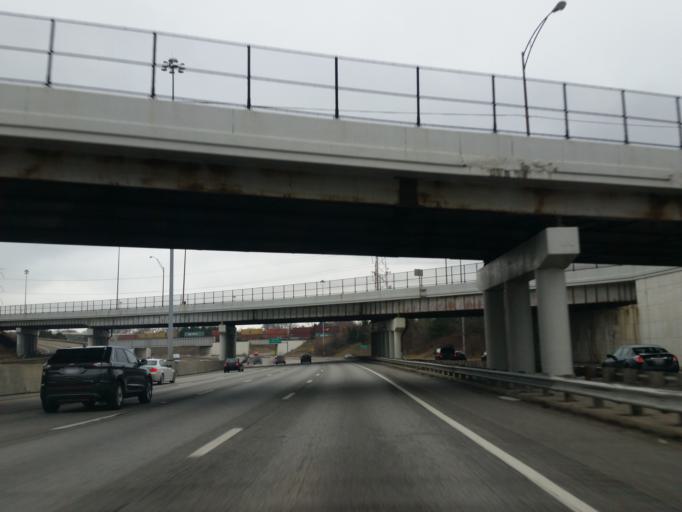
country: US
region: Ohio
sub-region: Cuyahoga County
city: Brooklyn Heights
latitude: 41.4190
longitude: -81.6794
